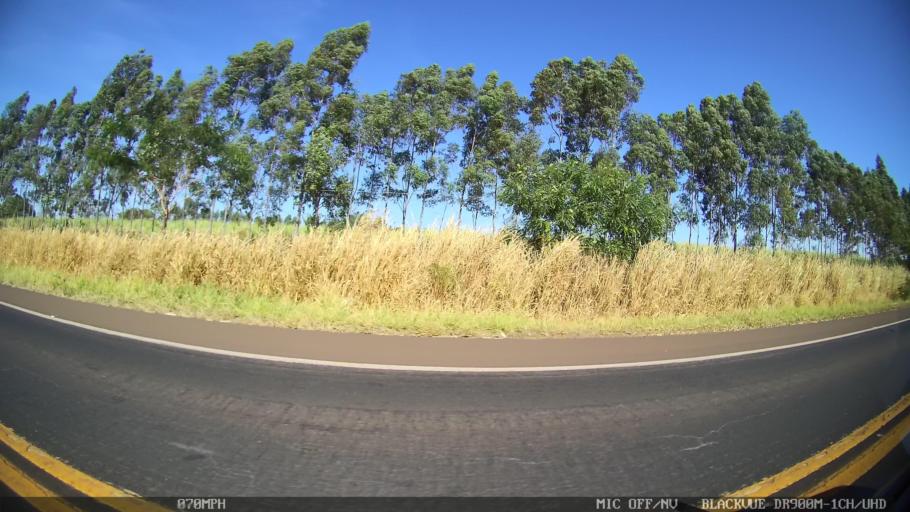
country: BR
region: Sao Paulo
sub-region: Olimpia
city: Olimpia
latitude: -20.6226
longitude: -48.7716
